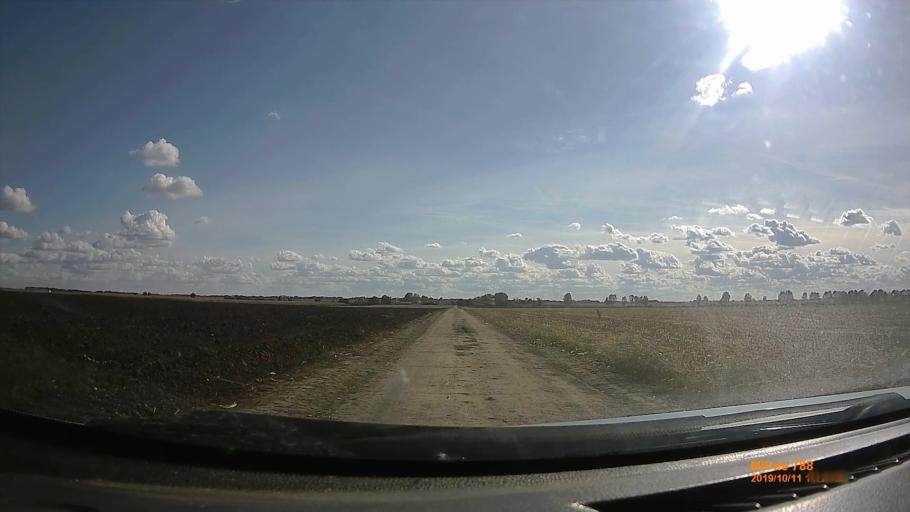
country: HU
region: Hajdu-Bihar
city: Hajduszoboszlo
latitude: 47.5375
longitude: 21.4012
